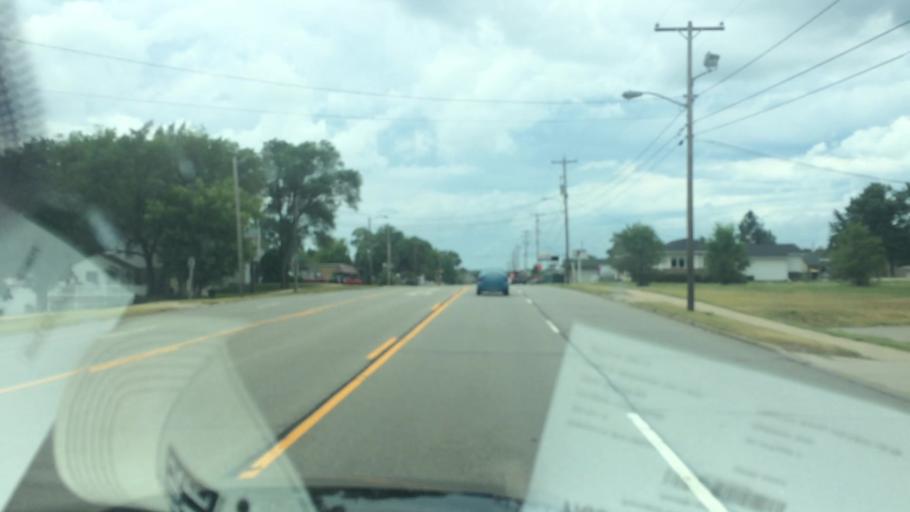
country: US
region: Wisconsin
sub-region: Marathon County
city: Schofield
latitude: 44.9038
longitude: -89.6071
